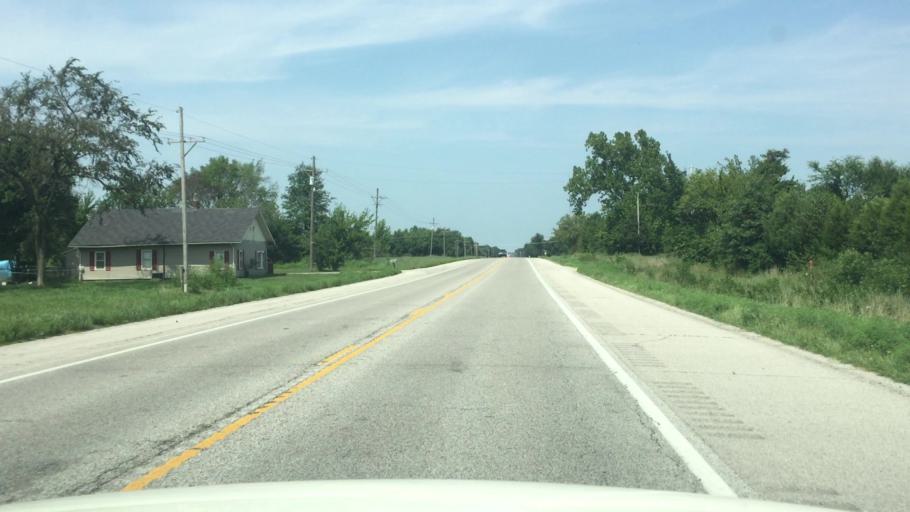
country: US
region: Kansas
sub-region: Cherokee County
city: Galena
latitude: 37.1166
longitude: -94.7043
